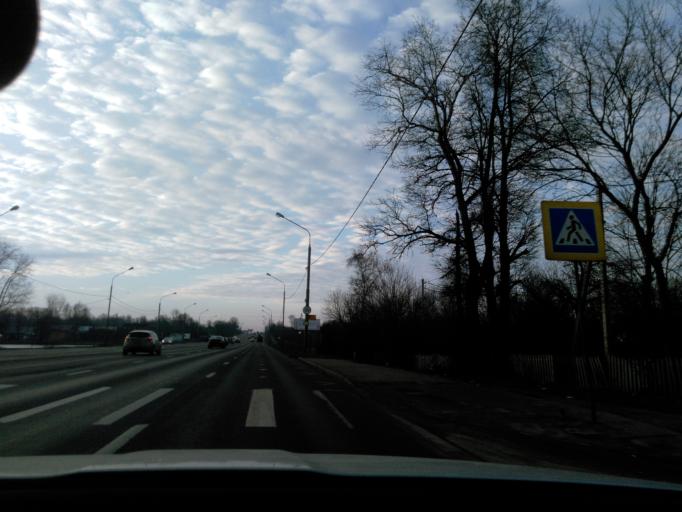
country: RU
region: Moskovskaya
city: Novopodrezkovo
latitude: 55.9314
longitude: 37.3776
